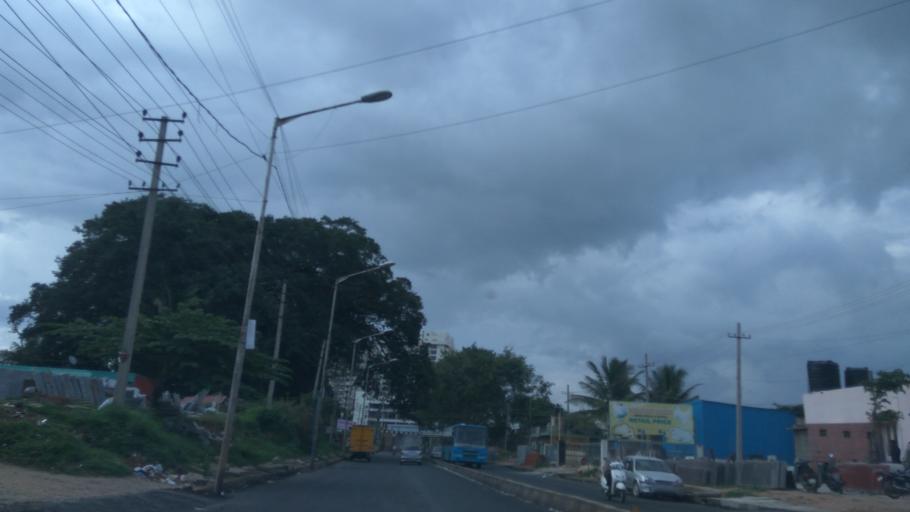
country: IN
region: Karnataka
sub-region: Bangalore Urban
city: Yelahanka
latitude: 13.0577
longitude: 77.6329
